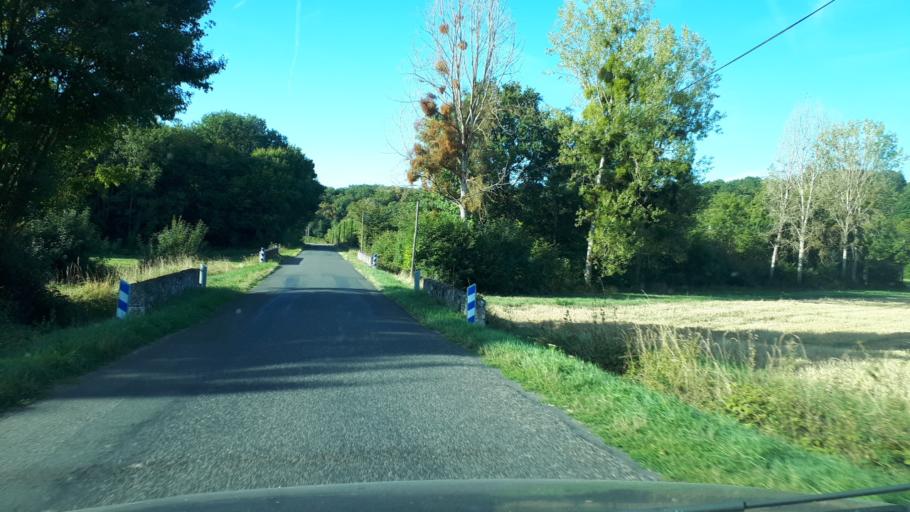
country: FR
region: Centre
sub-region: Departement d'Indre-et-Loire
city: Chateau-Renault
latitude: 47.6561
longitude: 0.9396
